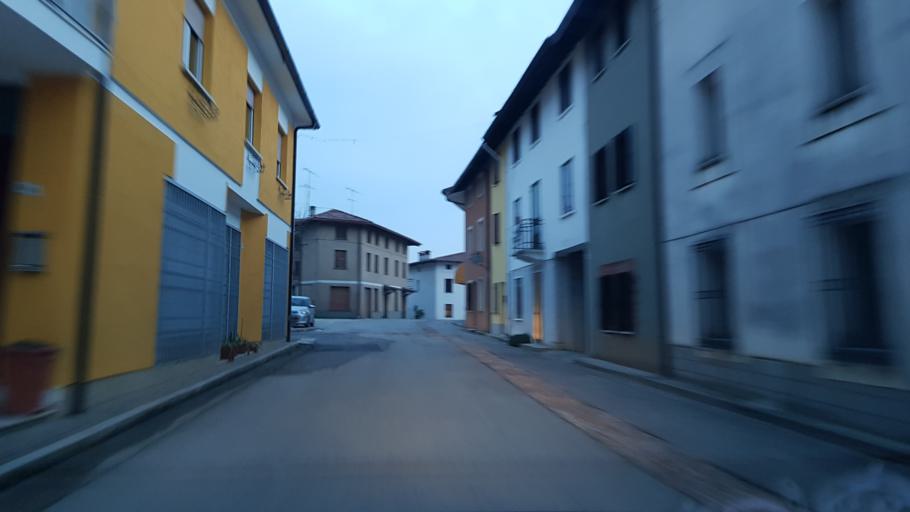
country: IT
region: Friuli Venezia Giulia
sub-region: Provincia di Udine
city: Attimis
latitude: 46.1899
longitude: 13.3085
